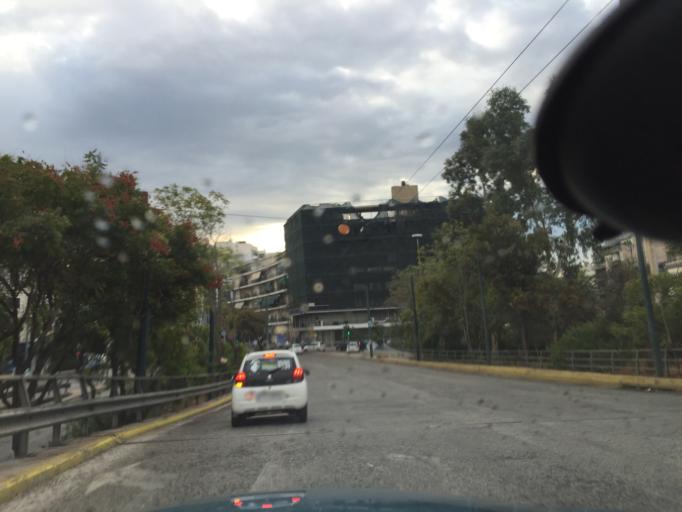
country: GR
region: Attica
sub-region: Nomarchia Athinas
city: Nea Smyrni
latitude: 37.9617
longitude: 23.7182
